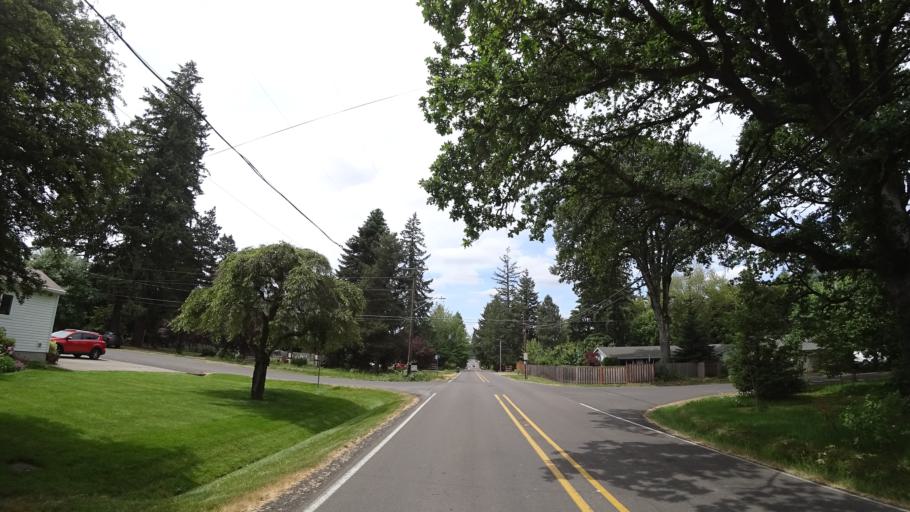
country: US
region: Oregon
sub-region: Washington County
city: Metzger
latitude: 45.4466
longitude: -122.7613
